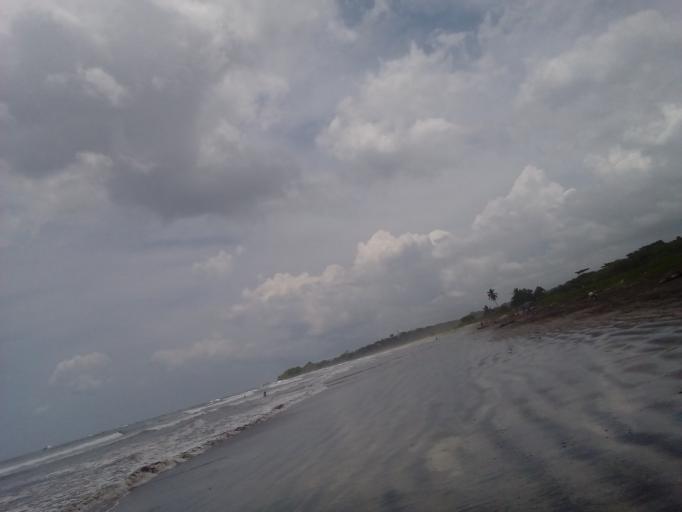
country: CR
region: Guanacaste
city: Samara
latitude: 9.9387
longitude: -85.6672
